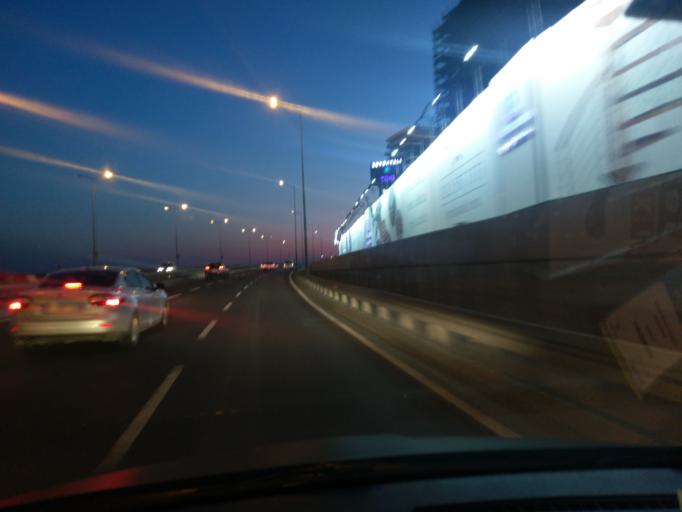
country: TR
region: Istanbul
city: Zeytinburnu
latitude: 40.9823
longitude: 28.9075
